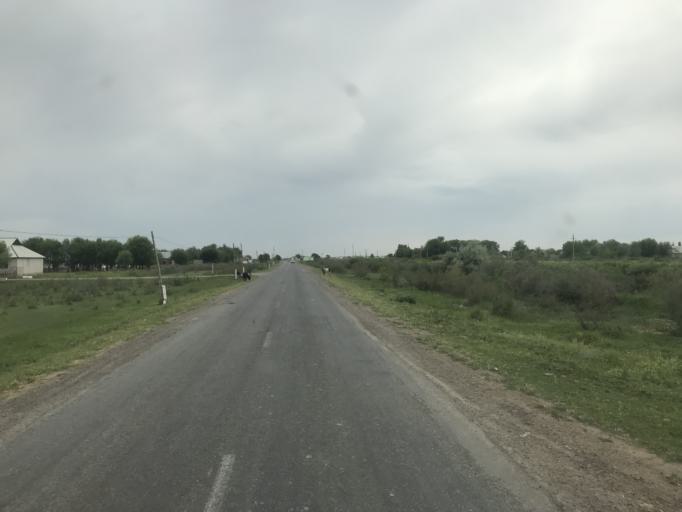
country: KZ
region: Ongtustik Qazaqstan
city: Asykata
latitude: 40.9152
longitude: 68.3957
